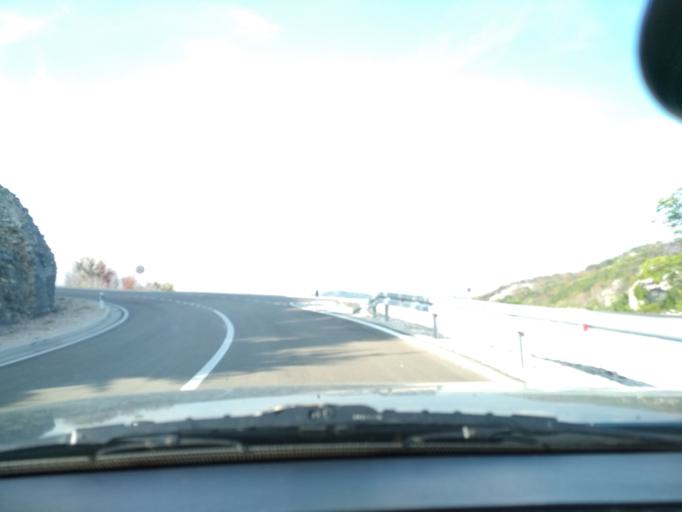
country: ME
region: Cetinje
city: Cetinje
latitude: 42.4355
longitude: 18.8577
